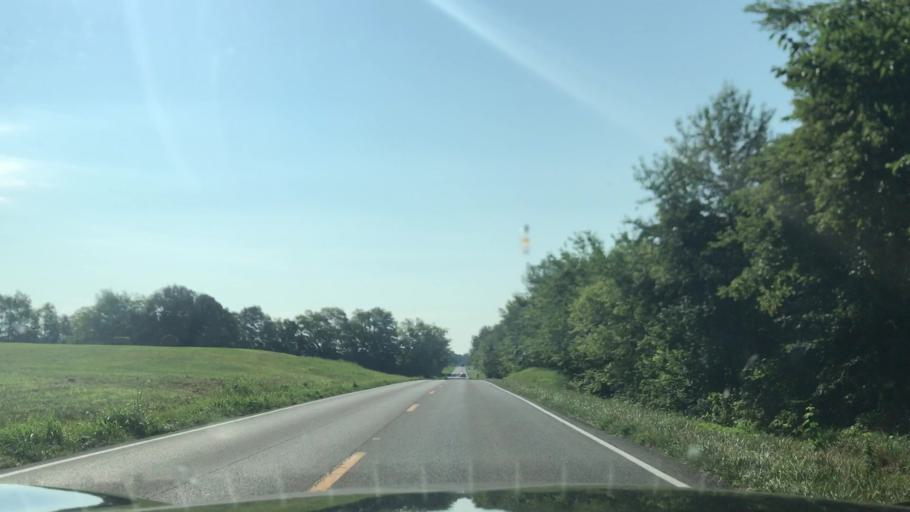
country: US
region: Kentucky
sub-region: Hart County
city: Horse Cave
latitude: 37.1721
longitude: -85.8582
